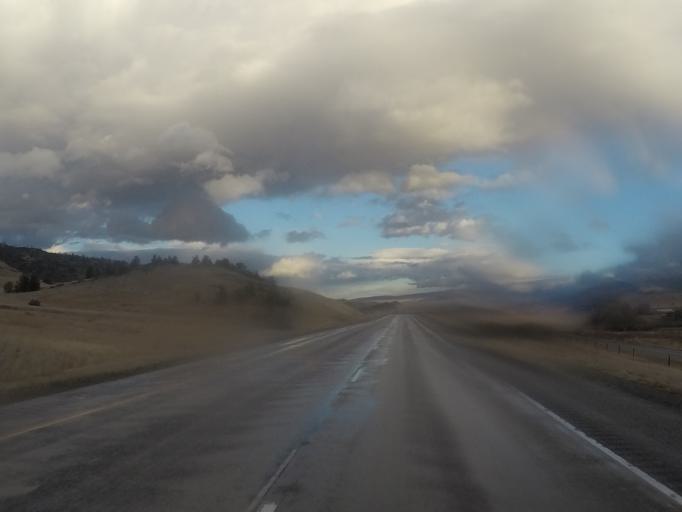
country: US
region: Montana
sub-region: Park County
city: Livingston
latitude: 45.6599
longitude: -110.6591
